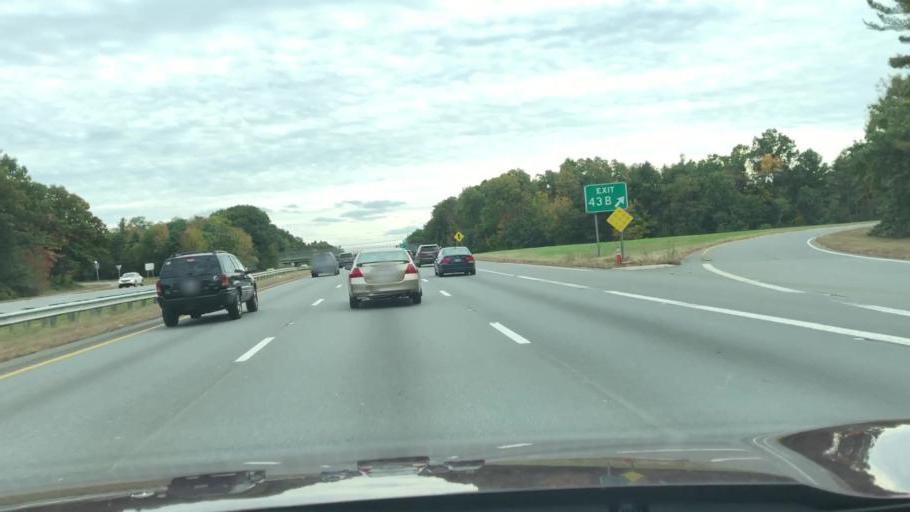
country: US
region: Massachusetts
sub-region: Essex County
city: Andover
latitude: 42.6491
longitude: -71.1876
